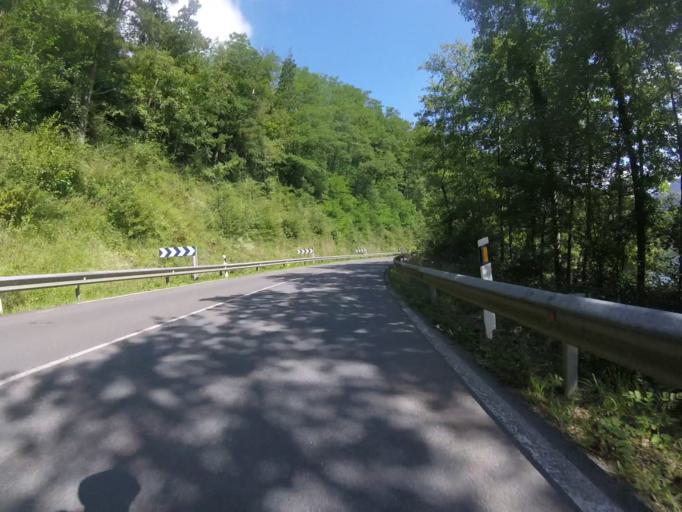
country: ES
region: Basque Country
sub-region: Provincia de Guipuzcoa
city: Beizama
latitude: 43.1154
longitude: -2.2294
